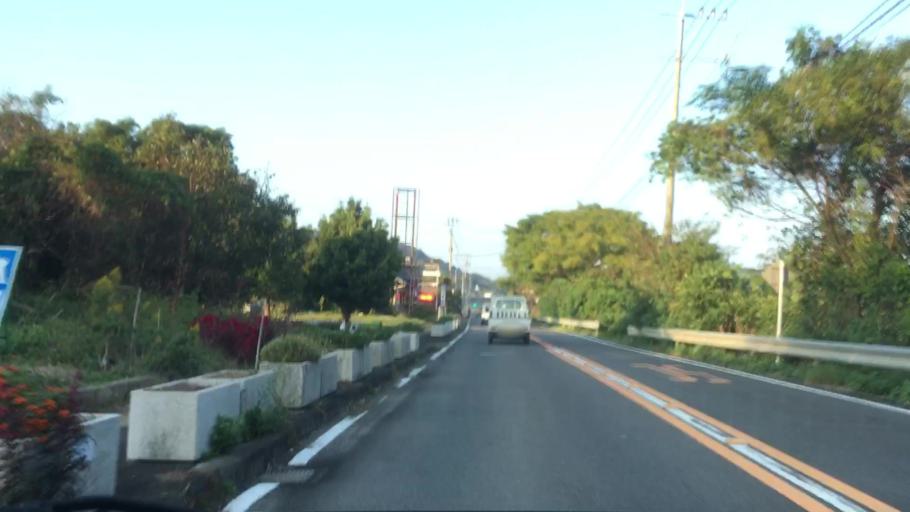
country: JP
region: Nagasaki
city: Sasebo
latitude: 33.0184
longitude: 129.7360
